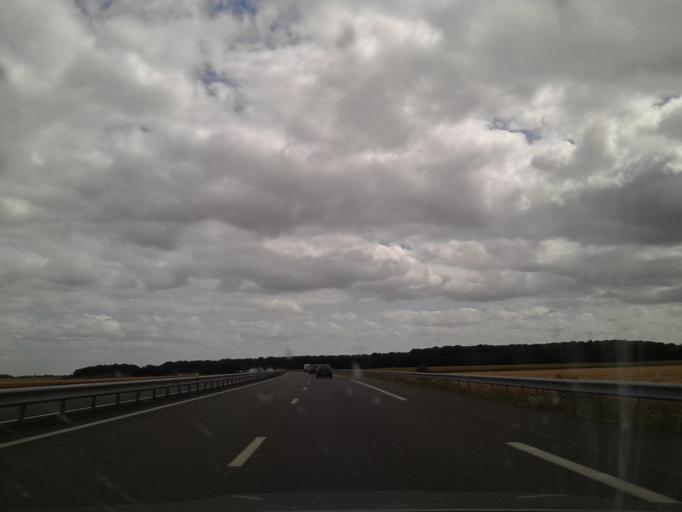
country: FR
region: Centre
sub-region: Departement du Cher
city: Levet
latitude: 46.9467
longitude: 2.4163
